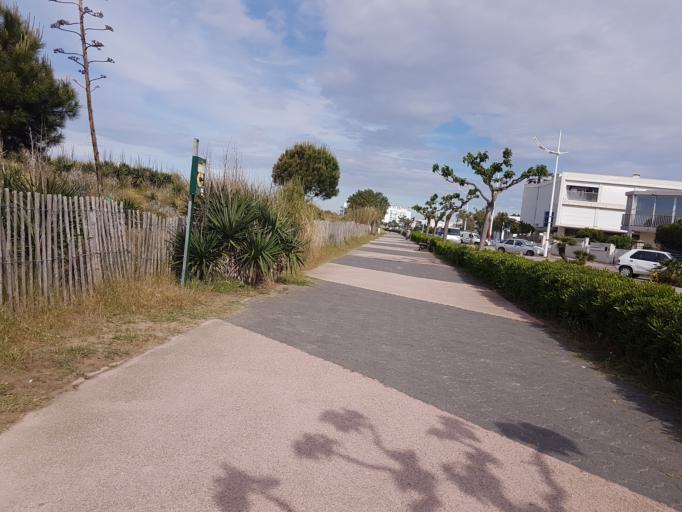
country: FR
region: Languedoc-Roussillon
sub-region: Departement du Gard
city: Le Grau-du-Roi
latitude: 43.5449
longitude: 4.1274
